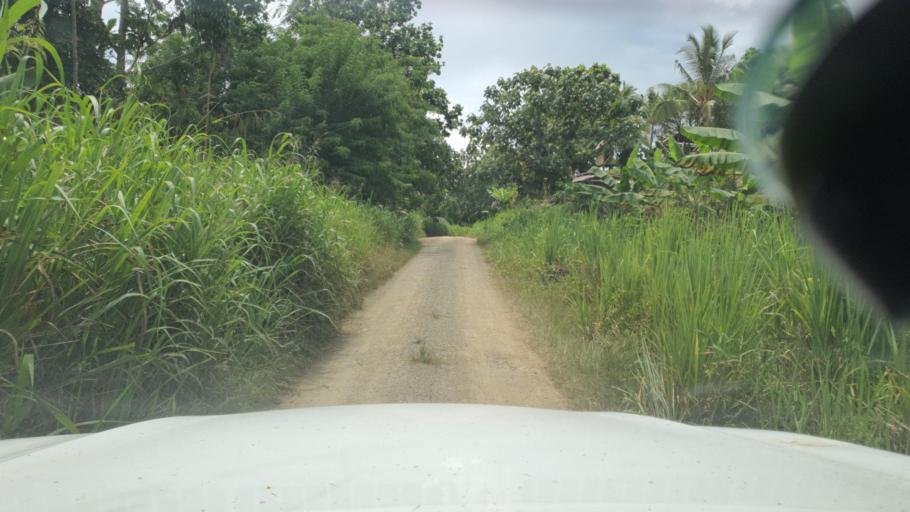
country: SB
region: Guadalcanal
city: Honiara
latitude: -9.4841
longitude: 160.3387
